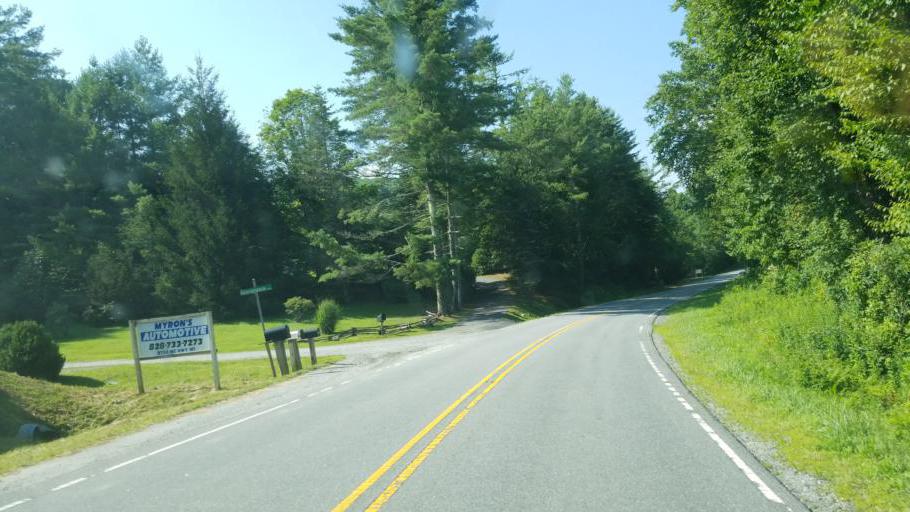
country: US
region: North Carolina
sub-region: Avery County
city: Newland
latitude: 35.9898
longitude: -81.8917
